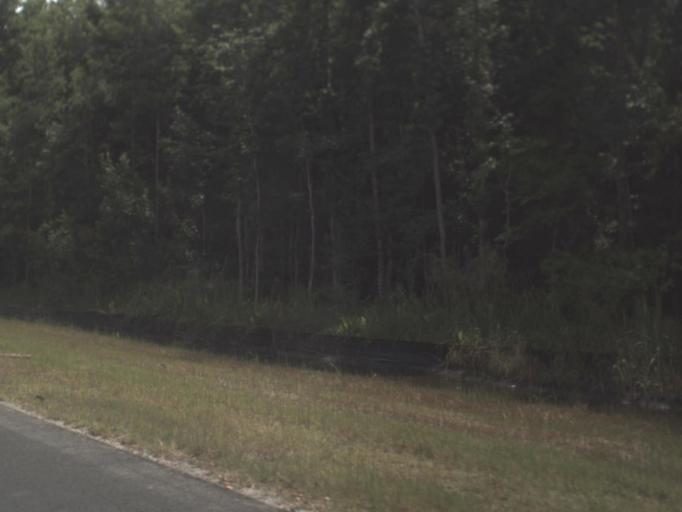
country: US
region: Florida
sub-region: Nassau County
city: Callahan
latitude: 30.5387
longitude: -81.8532
